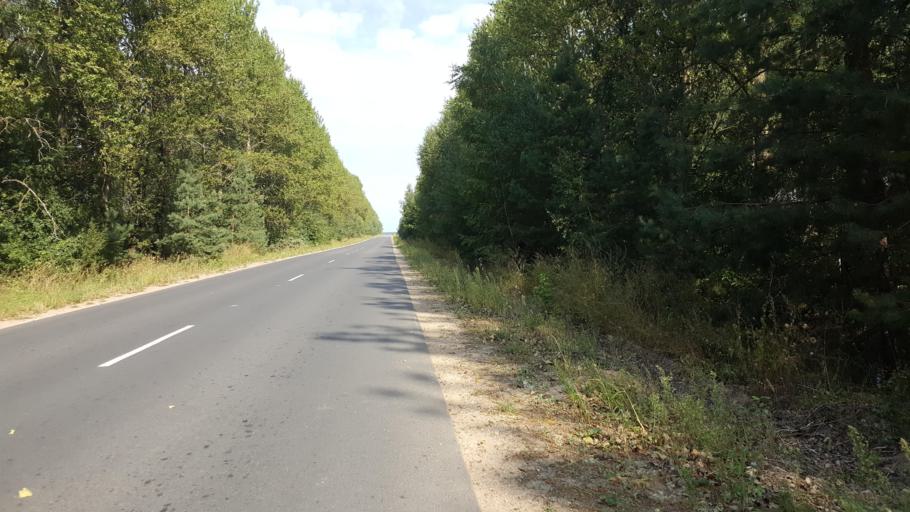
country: BY
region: Brest
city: Kamyanyets
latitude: 52.4509
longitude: 23.7370
